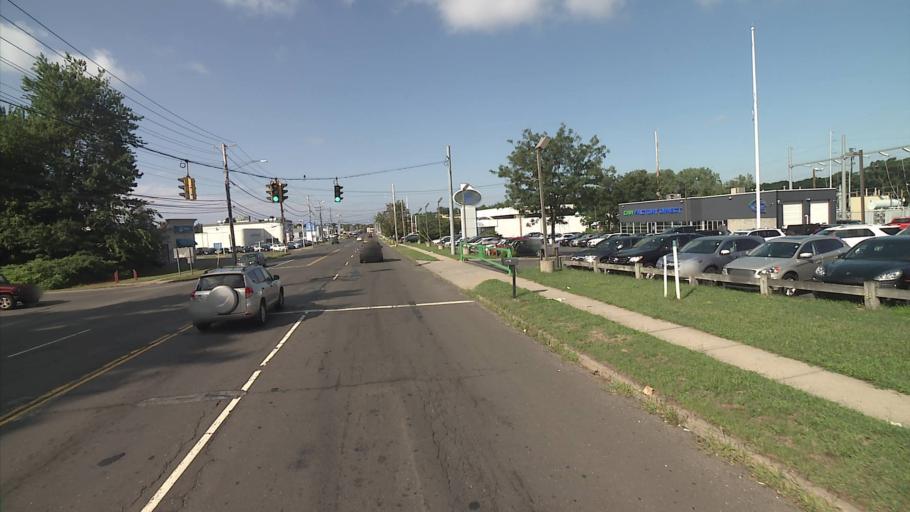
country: US
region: Connecticut
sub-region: New Haven County
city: City of Milford (balance)
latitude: 41.2119
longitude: -73.0798
